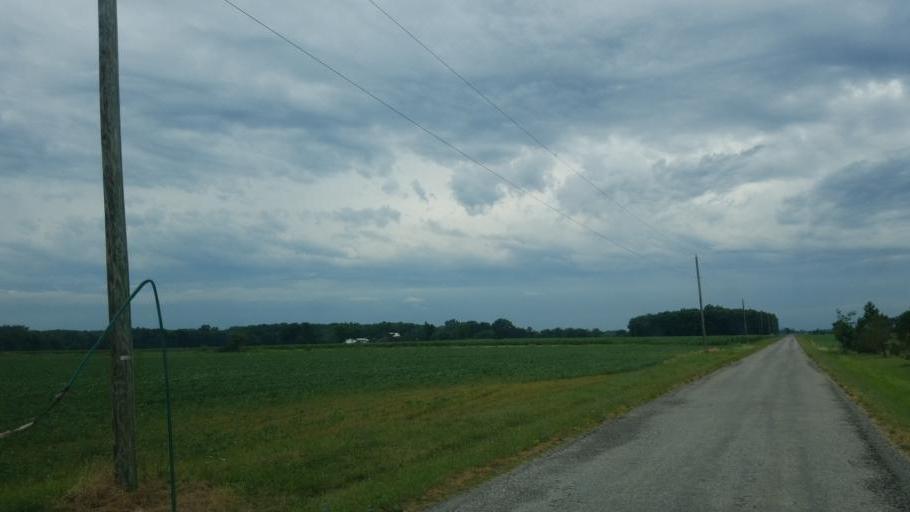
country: US
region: Ohio
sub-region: Paulding County
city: Antwerp
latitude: 41.2413
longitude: -84.6894
